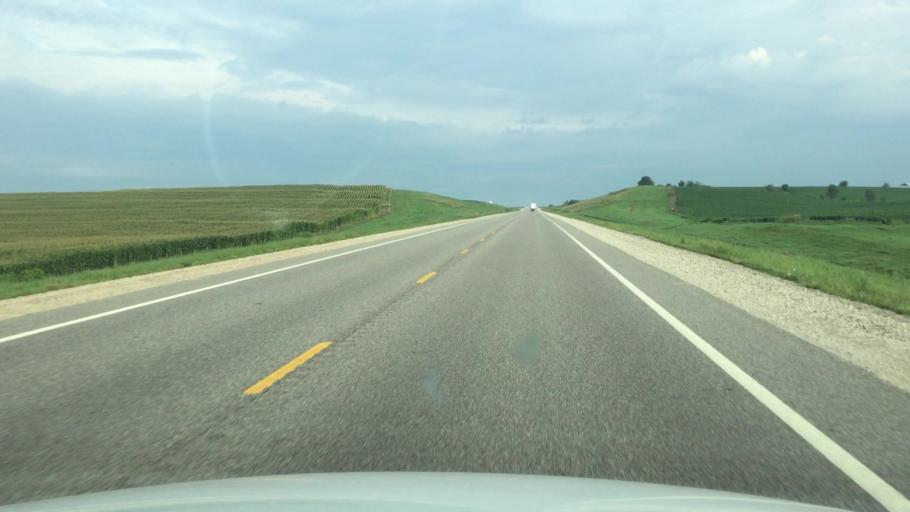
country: US
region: Kansas
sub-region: Doniphan County
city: Highland
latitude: 39.8207
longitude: -95.2112
